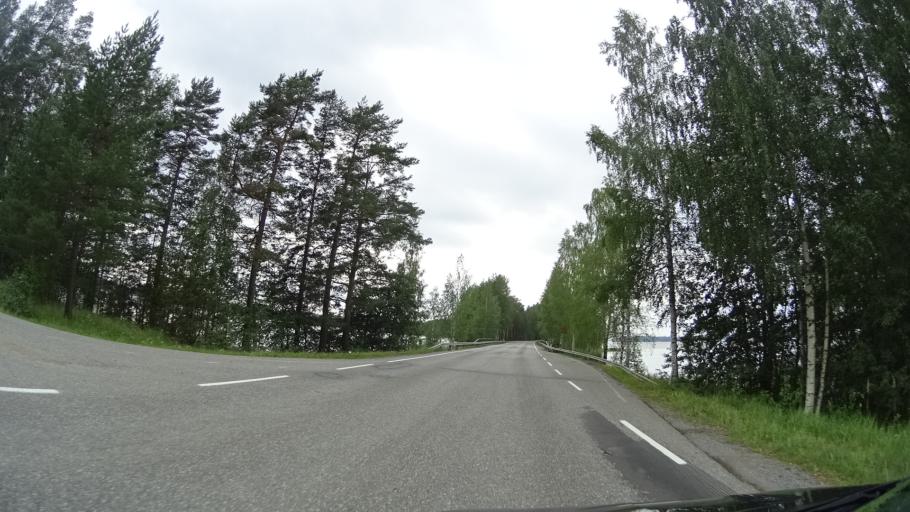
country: FI
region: Southern Savonia
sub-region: Savonlinna
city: Punkaharju
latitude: 61.7515
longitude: 29.4336
